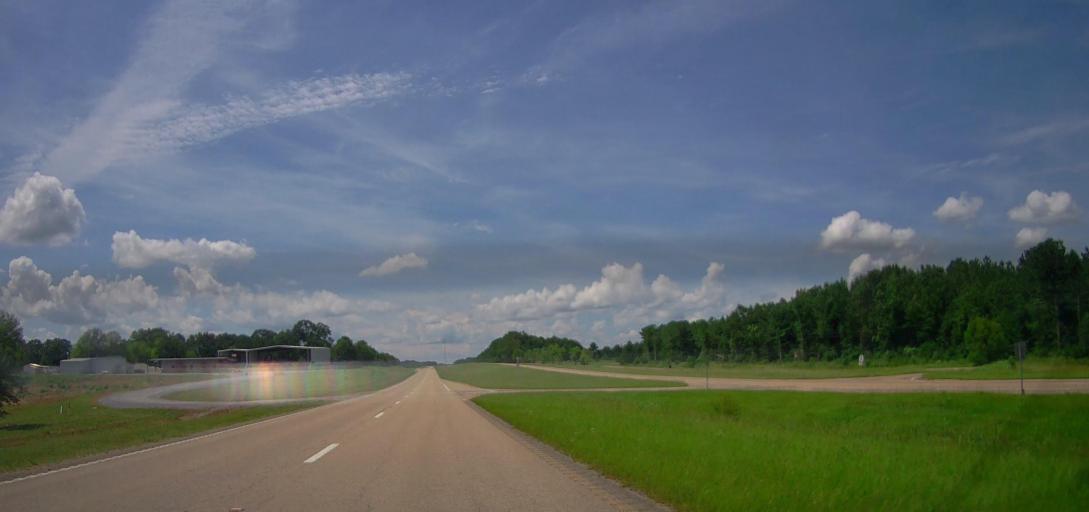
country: US
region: Mississippi
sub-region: Lee County
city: Nettleton
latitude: 33.9884
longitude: -88.6219
